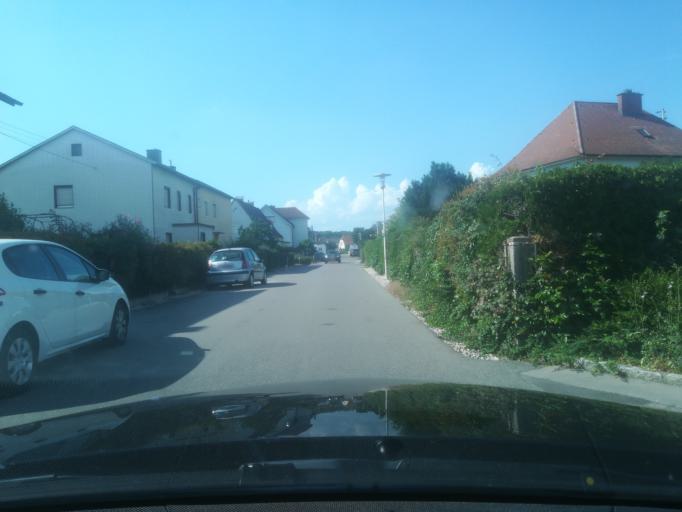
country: AT
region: Upper Austria
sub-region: Politischer Bezirk Linz-Land
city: Traun
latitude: 48.2410
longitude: 14.2451
